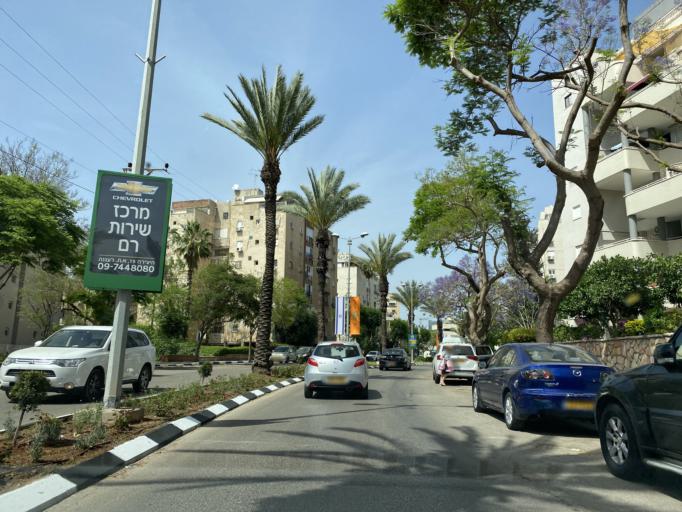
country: IL
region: Central District
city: Ra'anana
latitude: 32.1786
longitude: 34.8703
